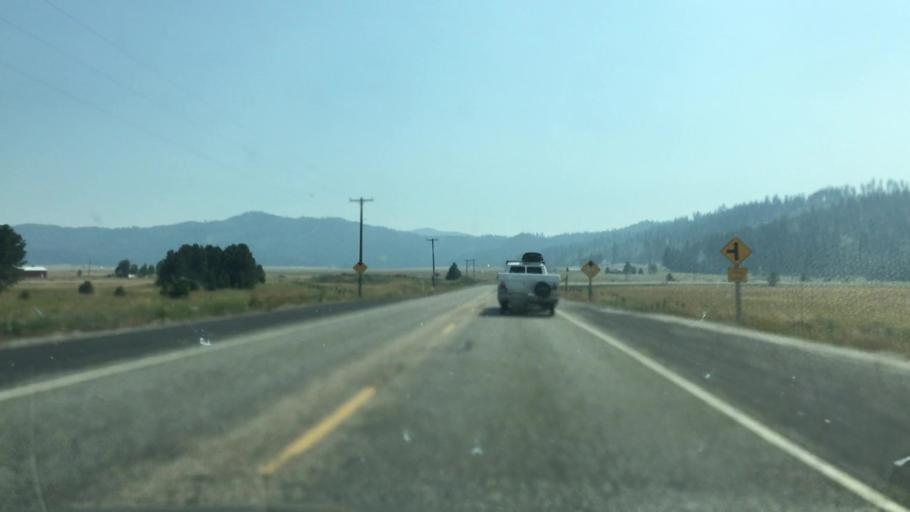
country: US
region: Idaho
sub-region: Valley County
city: Cascade
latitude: 44.3407
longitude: -116.0293
